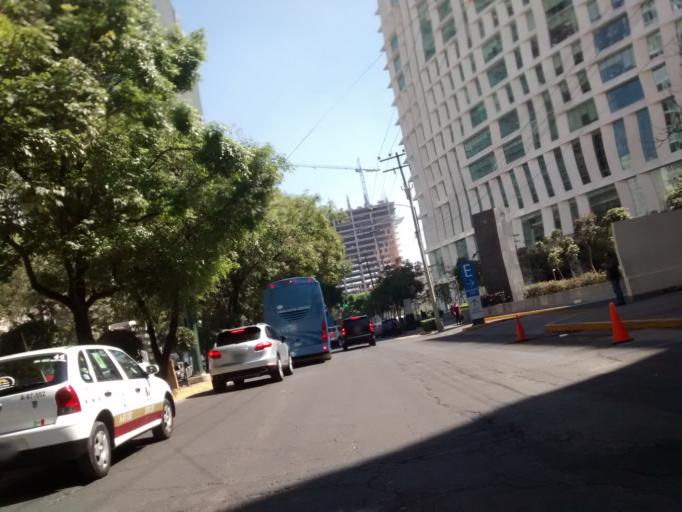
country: MX
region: Mexico City
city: Miguel Hidalgo
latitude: 19.4402
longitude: -99.2040
